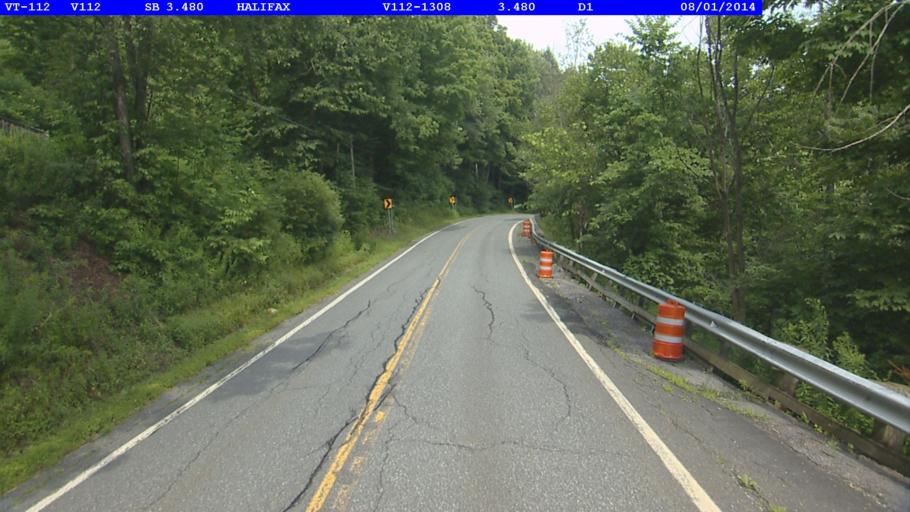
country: US
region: Massachusetts
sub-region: Franklin County
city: Colrain
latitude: 42.7627
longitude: -72.7727
